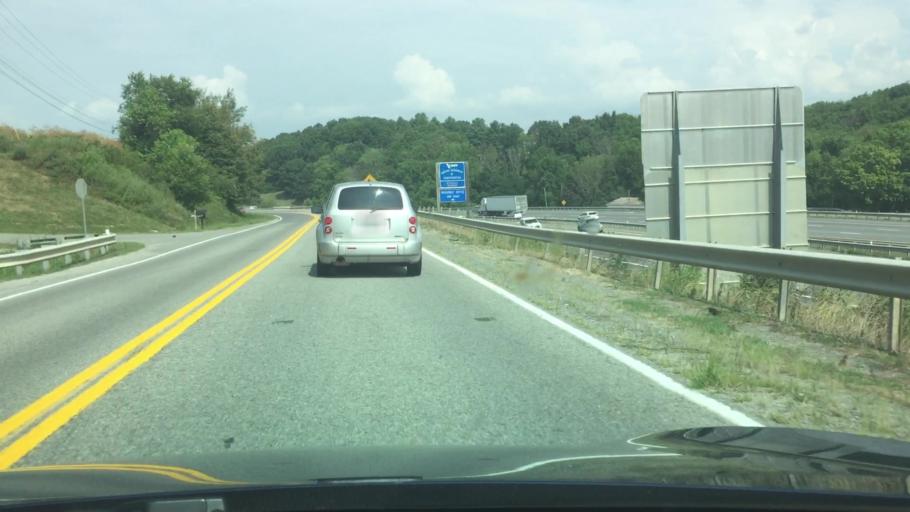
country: US
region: Virginia
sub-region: Wythe County
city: Wytheville
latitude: 36.9396
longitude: -81.0055
